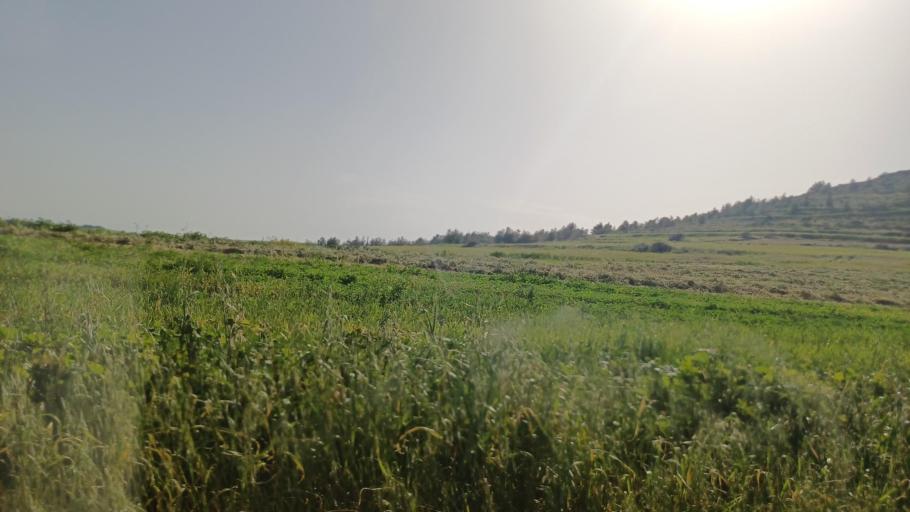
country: CY
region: Lefkosia
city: Astromeritis
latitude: 35.0950
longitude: 32.9516
